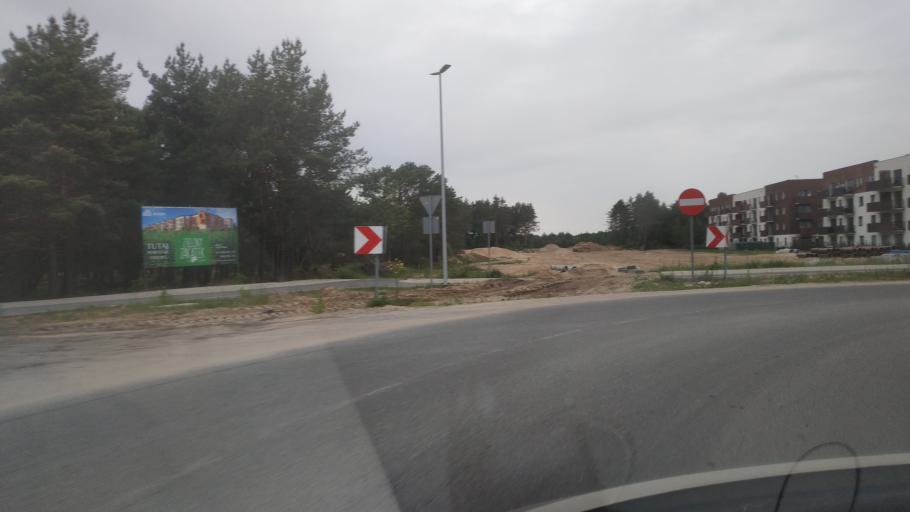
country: PL
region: Kujawsko-Pomorskie
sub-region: Powiat torunski
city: Lysomice
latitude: 53.0526
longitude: 18.6033
